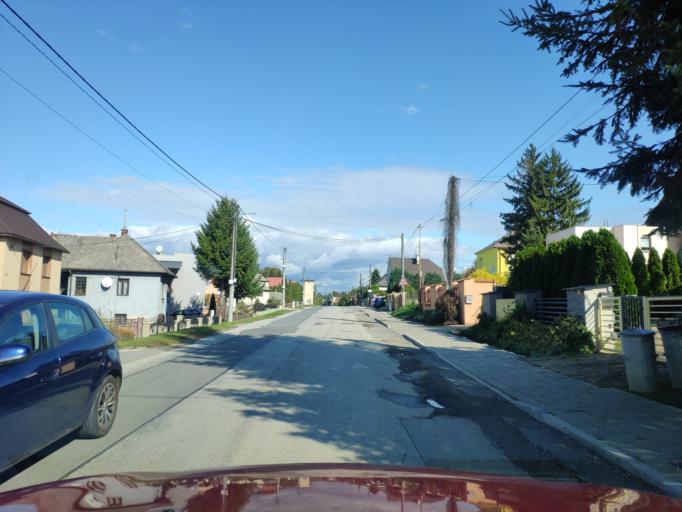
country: SK
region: Presovsky
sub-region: Okres Presov
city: Presov
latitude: 48.9152
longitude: 21.2604
